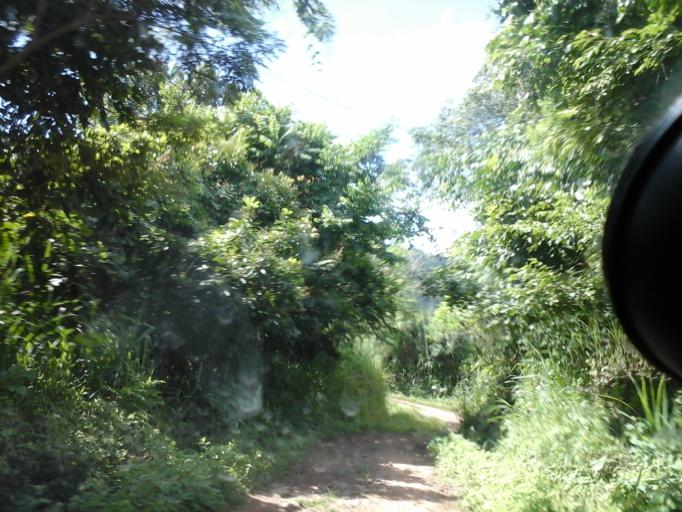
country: CO
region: Cesar
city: San Diego
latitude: 10.2721
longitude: -73.0930
